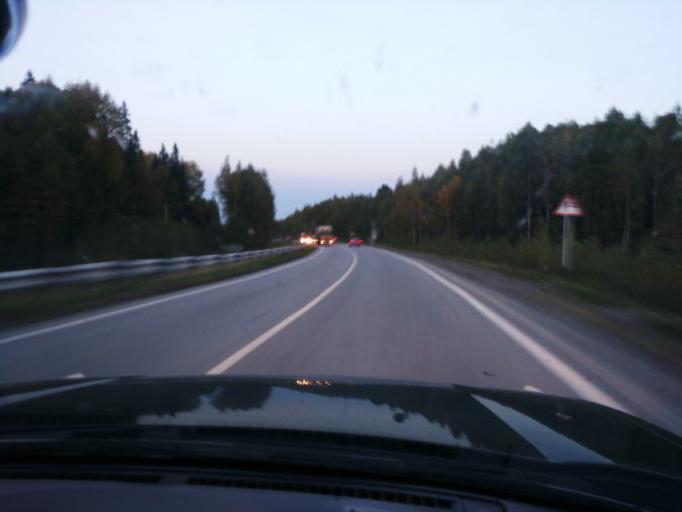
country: RU
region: Perm
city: Verkhnechusovskiye Gorodki
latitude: 58.2452
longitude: 57.0282
